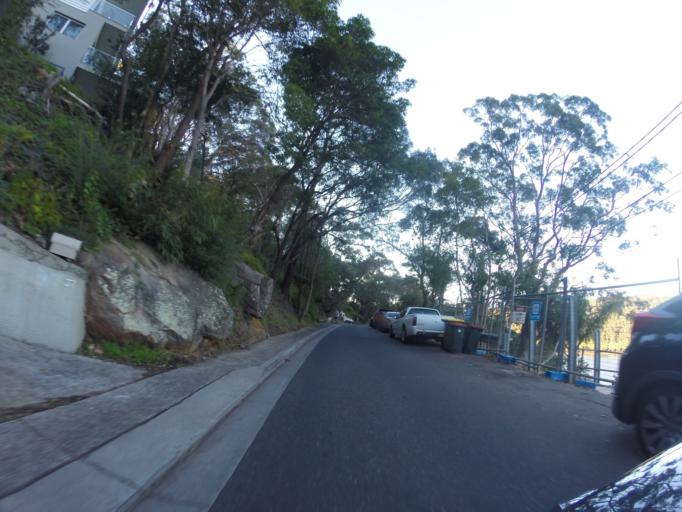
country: AU
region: New South Wales
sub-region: Sutherland Shire
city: Grays Point
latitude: -34.0613
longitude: 151.0846
